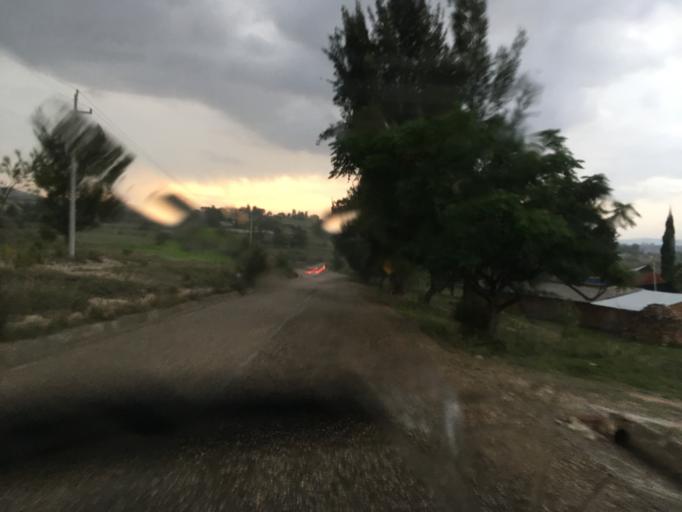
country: MX
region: Oaxaca
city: Santiago Tilantongo
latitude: 17.2854
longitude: -97.2878
